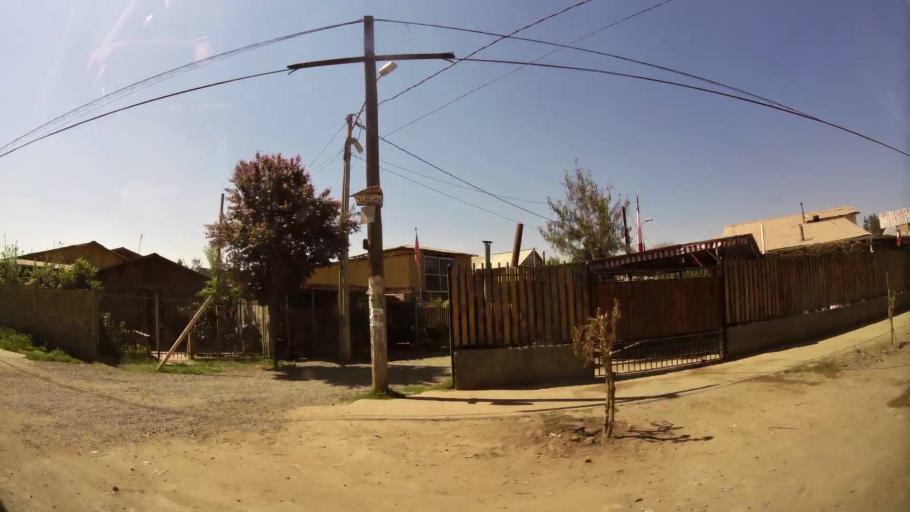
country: CL
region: Santiago Metropolitan
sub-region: Provincia de Talagante
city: Penaflor
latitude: -33.5867
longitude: -70.8074
